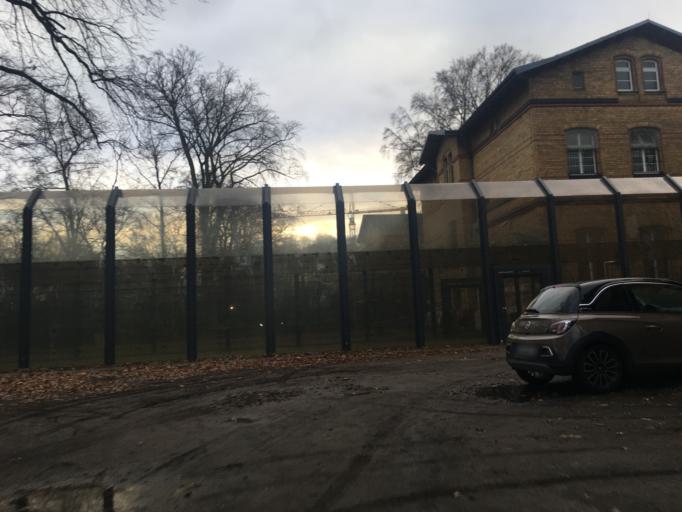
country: DE
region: Berlin
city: Wittenau
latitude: 52.5829
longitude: 13.3307
